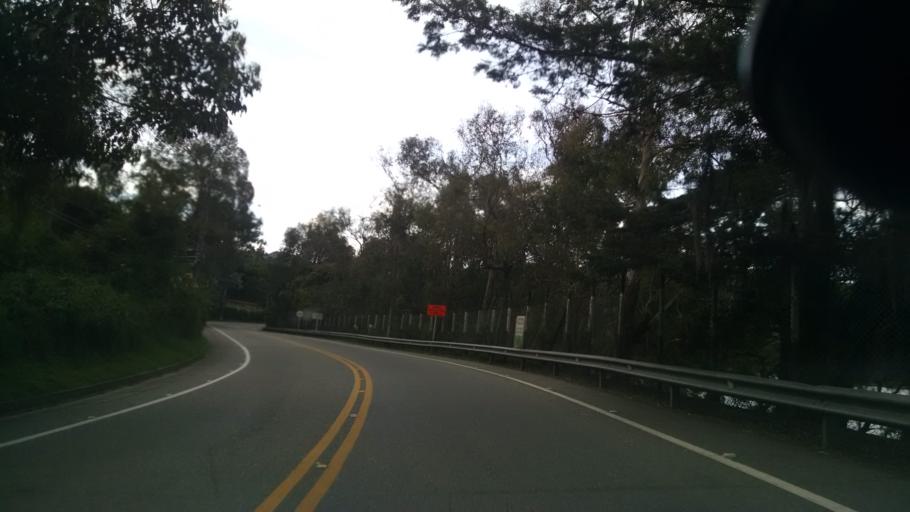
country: CO
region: Antioquia
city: El Retiro
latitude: 6.1050
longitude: -75.5026
